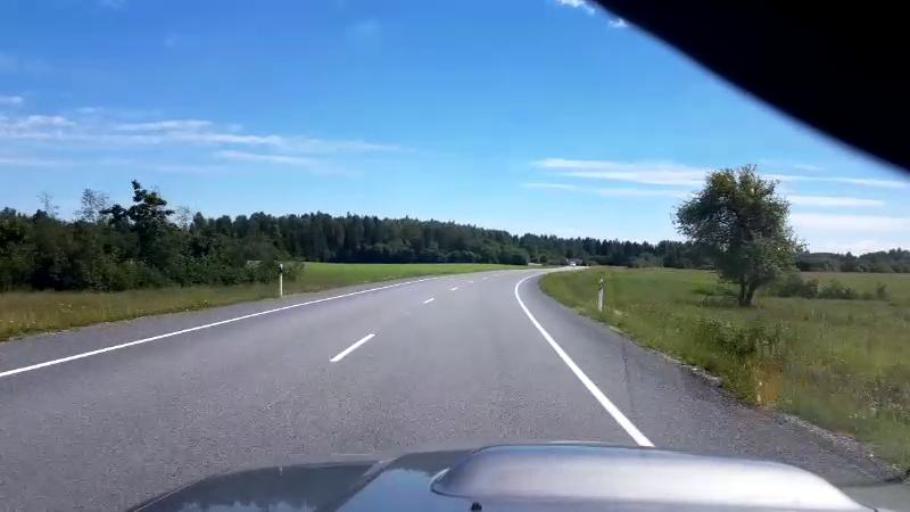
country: EE
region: Jaervamaa
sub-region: Jaerva-Jaani vald
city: Jarva-Jaani
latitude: 59.0008
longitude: 25.9373
